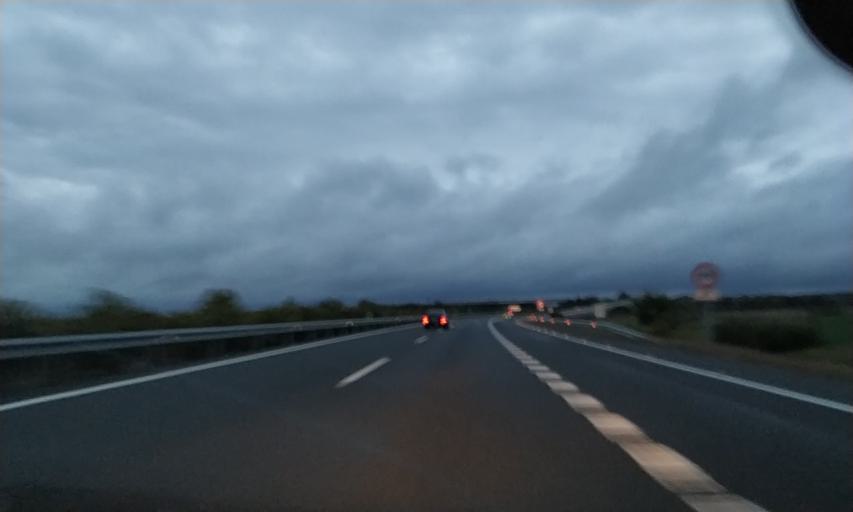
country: ES
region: Extremadura
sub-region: Provincia de Caceres
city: Casas de Don Antonio
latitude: 39.2265
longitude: -6.3005
